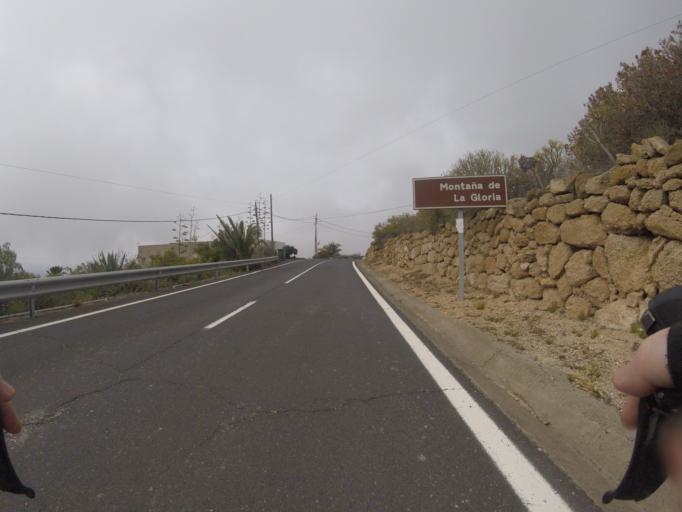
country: ES
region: Canary Islands
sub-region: Provincia de Santa Cruz de Tenerife
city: Fasnia
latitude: 28.2258
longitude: -16.4466
